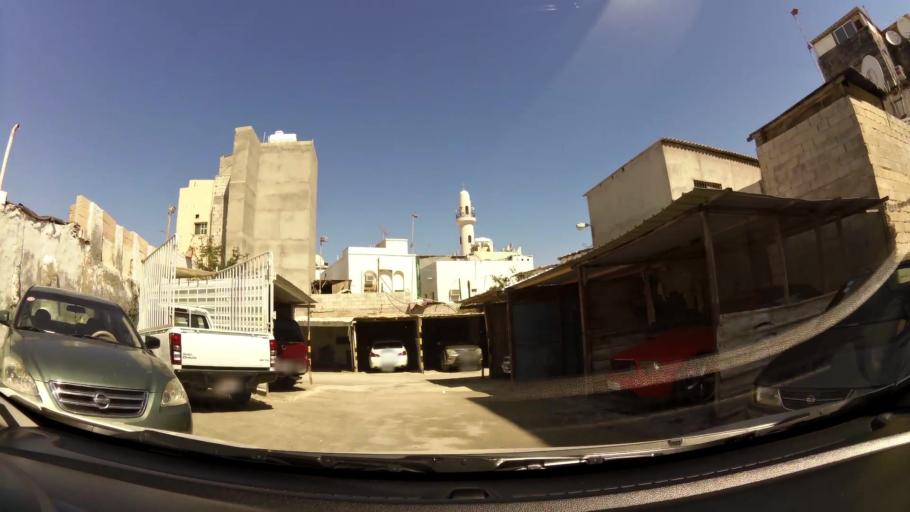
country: BH
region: Muharraq
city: Al Muharraq
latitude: 26.2550
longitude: 50.6115
